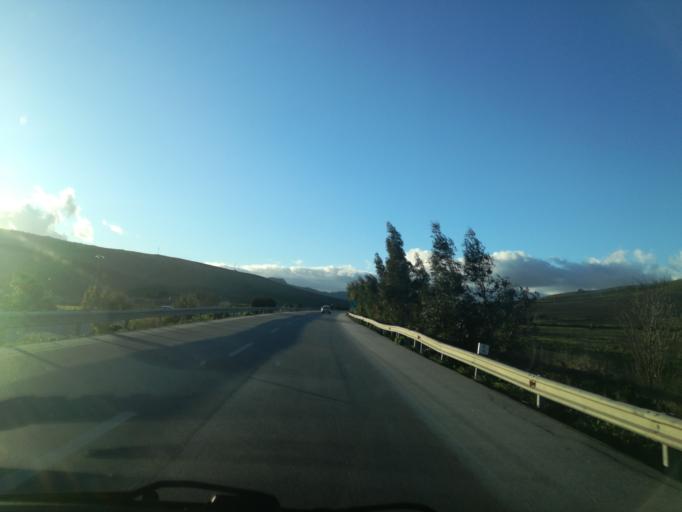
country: IT
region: Sicily
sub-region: Palermo
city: Castellana Sicula
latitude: 37.7384
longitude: 14.0097
